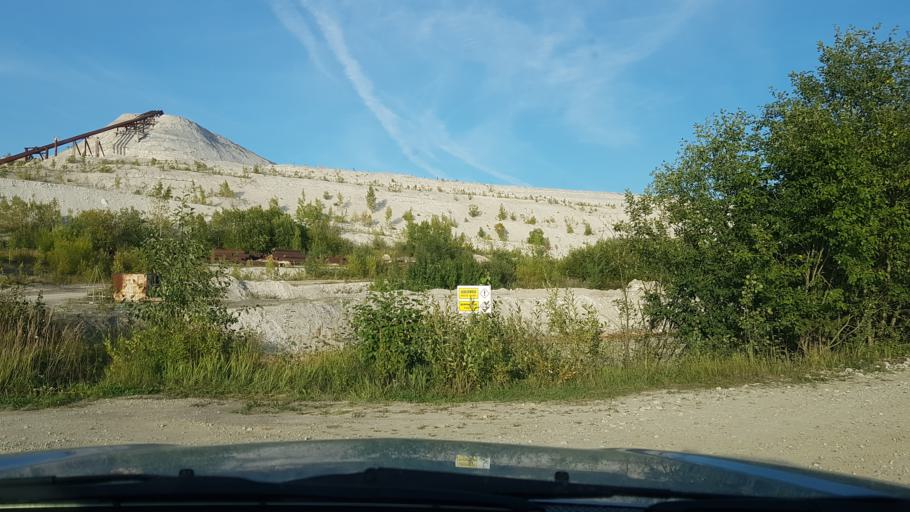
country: EE
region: Ida-Virumaa
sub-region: Sillamaee linn
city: Sillamae
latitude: 59.2777
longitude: 27.9222
